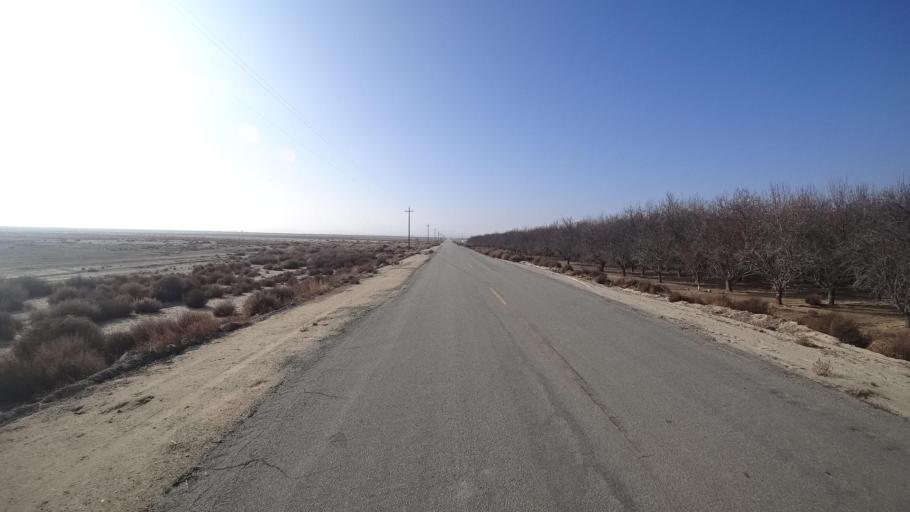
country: US
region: California
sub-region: Kern County
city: Maricopa
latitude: 35.1012
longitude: -119.3546
